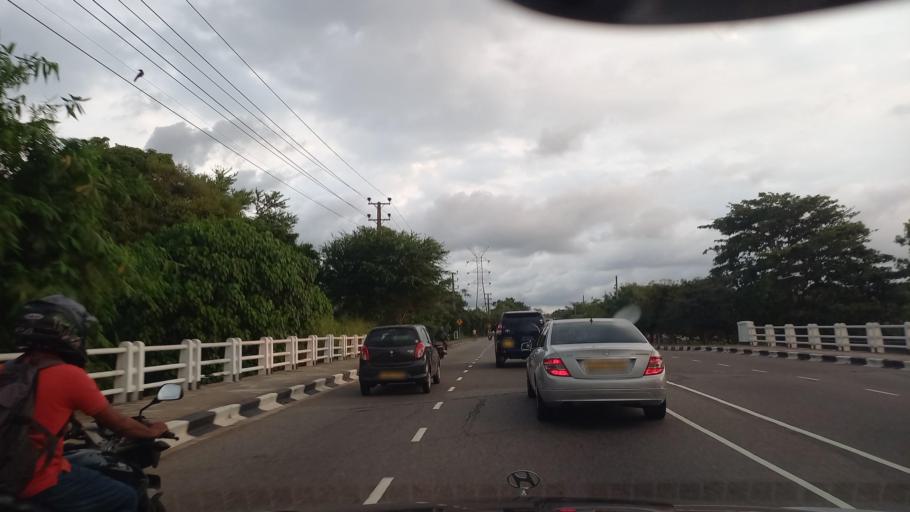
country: LK
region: Western
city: Battaramulla South
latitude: 6.8792
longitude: 79.9284
